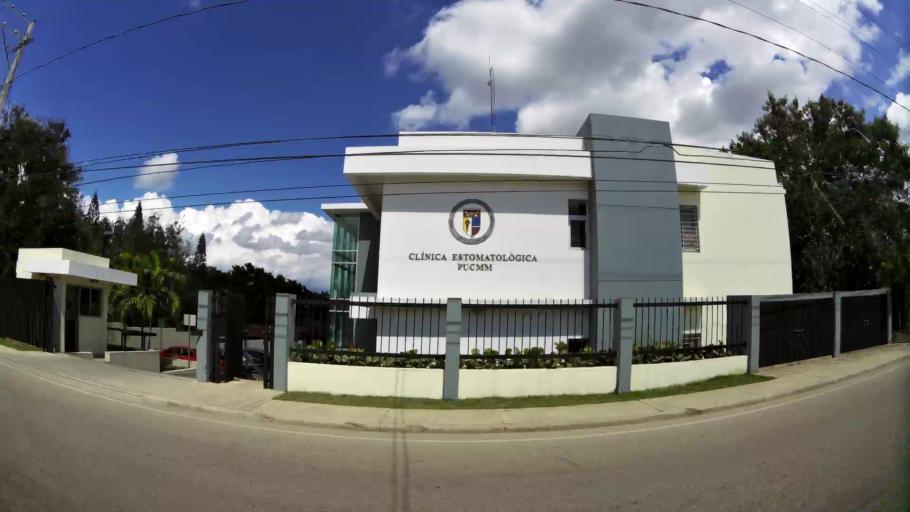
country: DO
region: Santiago
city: Santiago de los Caballeros
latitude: 19.4159
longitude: -70.6777
